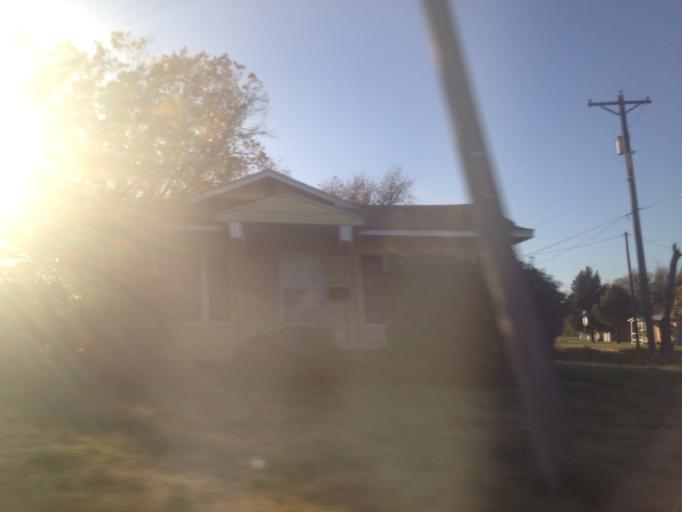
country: US
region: Texas
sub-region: Taylor County
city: Abilene
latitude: 32.4376
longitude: -99.7595
